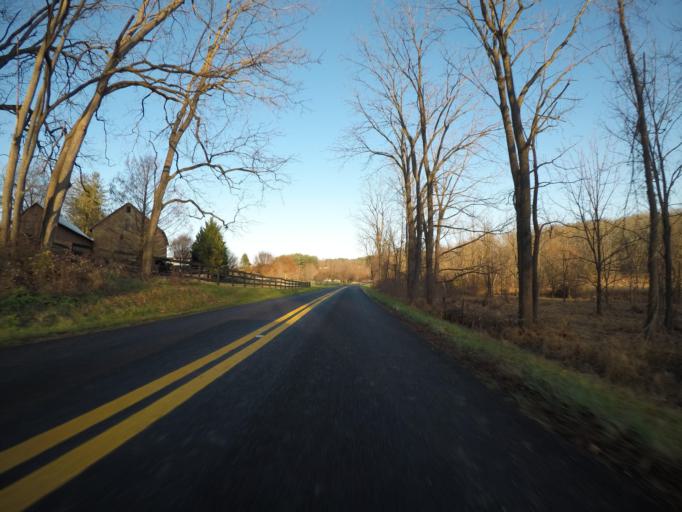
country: US
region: Maryland
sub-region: Carroll County
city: Hampstead
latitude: 39.5882
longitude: -76.8971
